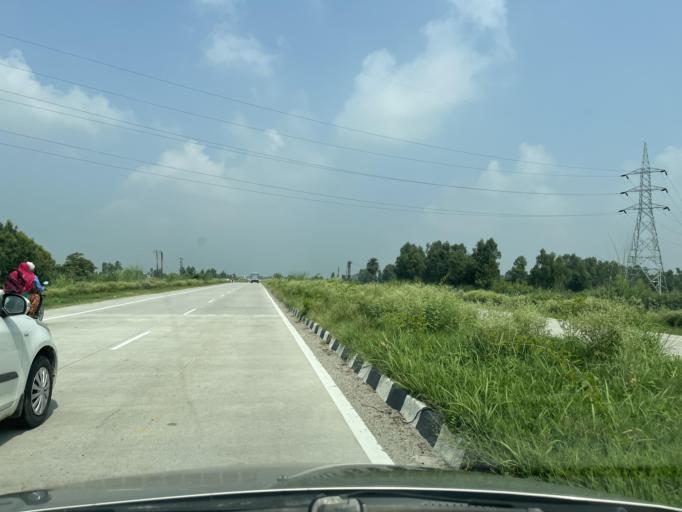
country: IN
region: Uttarakhand
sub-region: Udham Singh Nagar
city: Kashipur
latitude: 29.1664
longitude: 78.9578
